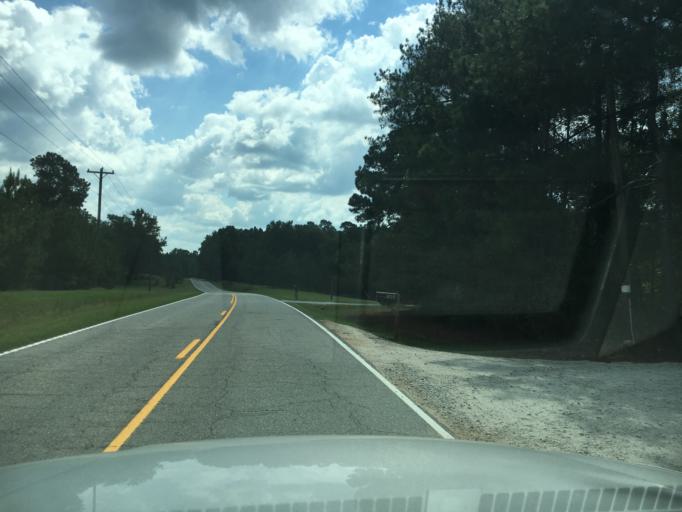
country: US
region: South Carolina
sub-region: Greenwood County
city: Greenwood
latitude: 34.1192
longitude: -82.1269
